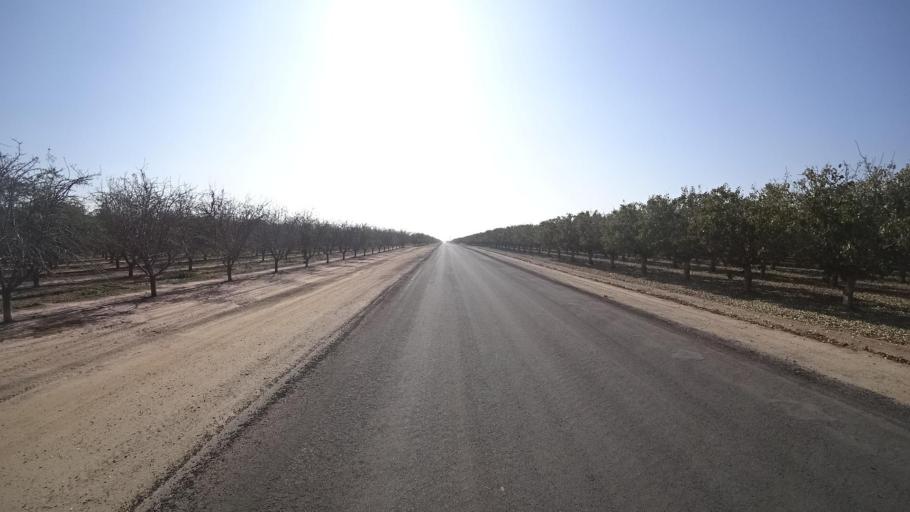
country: US
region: California
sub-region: Kern County
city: McFarland
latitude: 35.6574
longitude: -119.1868
